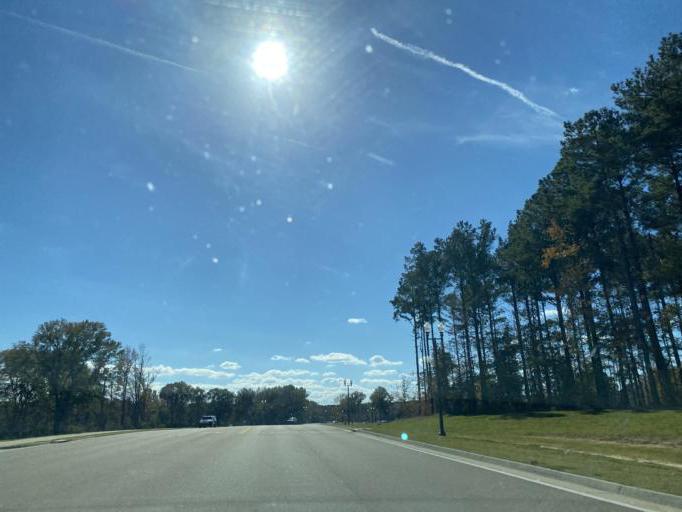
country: US
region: Mississippi
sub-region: Madison County
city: Madison
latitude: 32.4645
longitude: -90.1271
